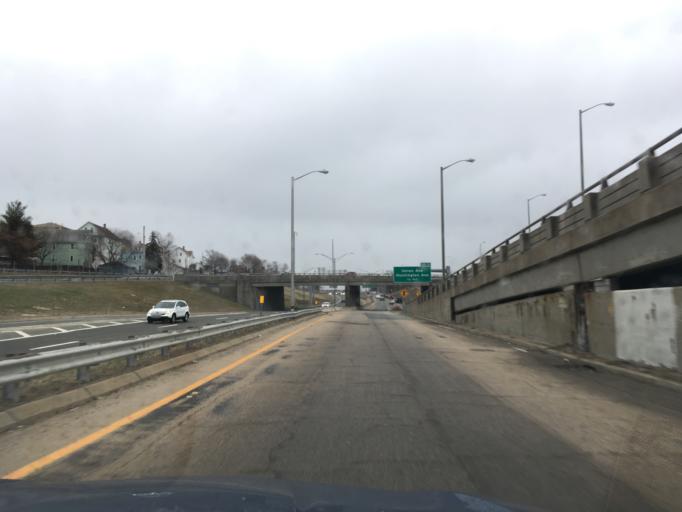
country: US
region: Rhode Island
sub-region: Providence County
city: Providence
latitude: 41.8150
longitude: -71.4397
